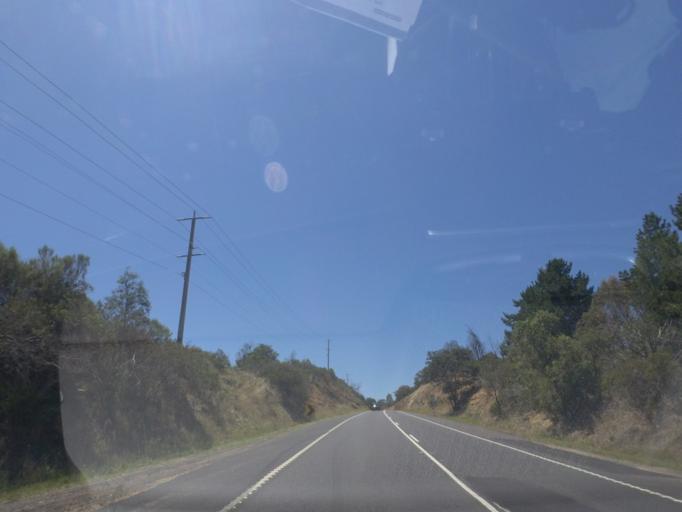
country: AU
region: Victoria
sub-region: Whittlesea
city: Whittlesea
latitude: -37.4588
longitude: 145.0315
